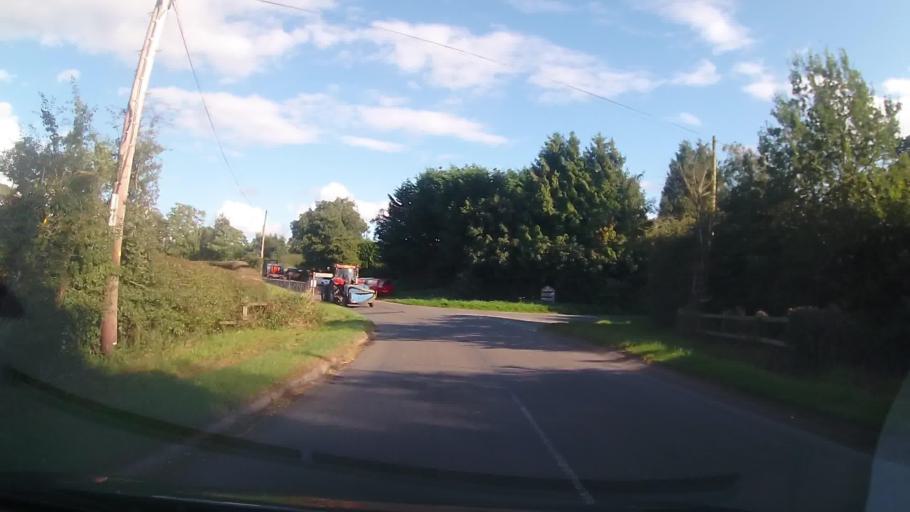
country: GB
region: England
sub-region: Shropshire
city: Great Hanwood
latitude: 52.6517
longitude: -2.8013
